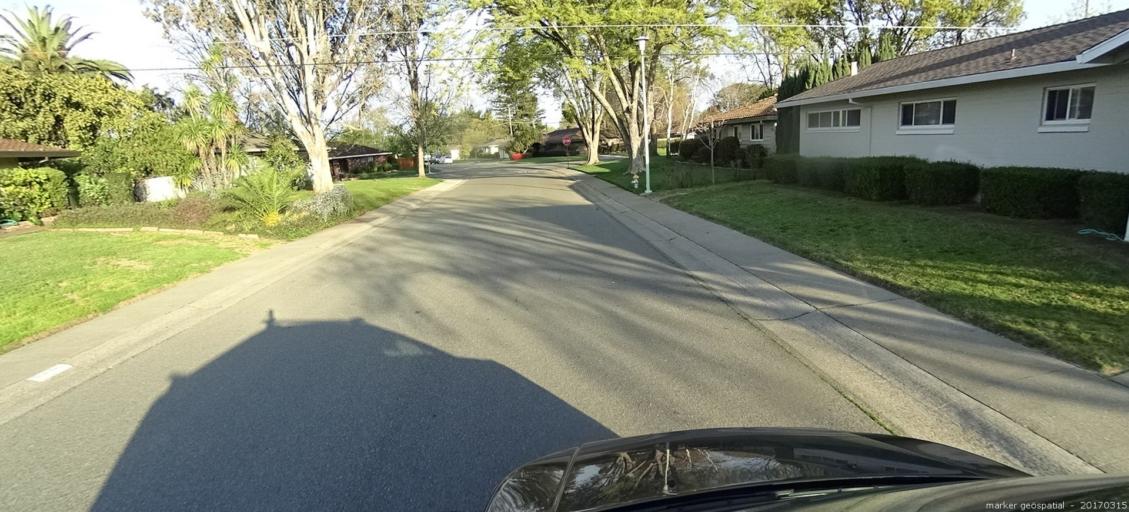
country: US
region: California
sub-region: Sacramento County
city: Parkway
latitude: 38.5074
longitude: -121.5104
